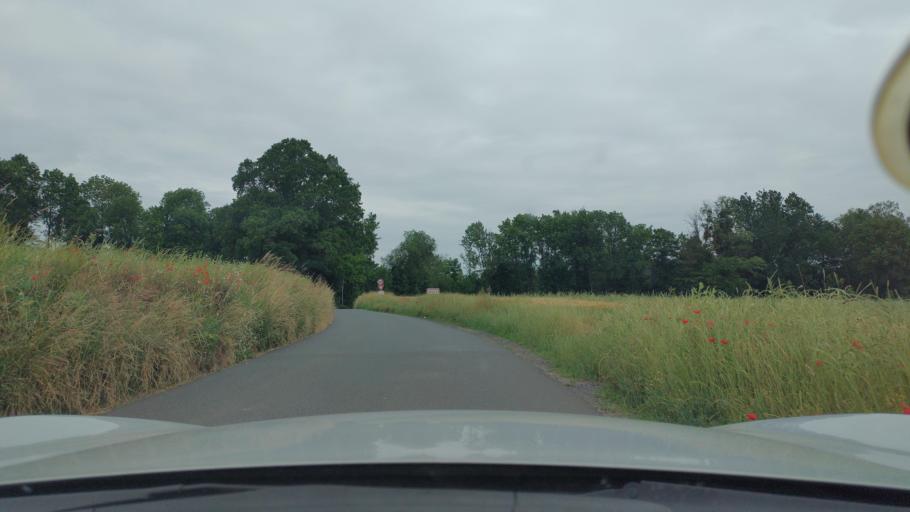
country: FR
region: Picardie
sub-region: Departement de l'Oise
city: Betz
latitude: 49.1506
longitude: 2.9614
